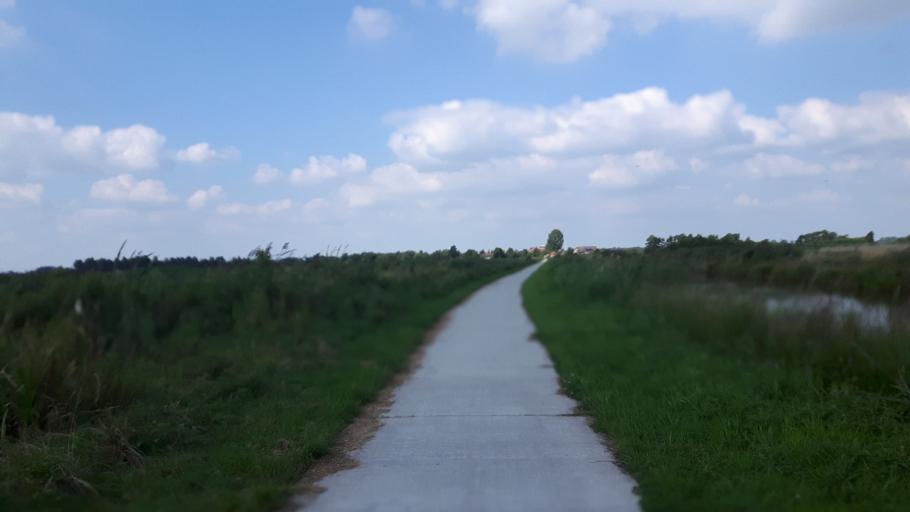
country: NL
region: Groningen
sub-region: Gemeente Leek
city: Leek
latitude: 53.1702
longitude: 6.4250
